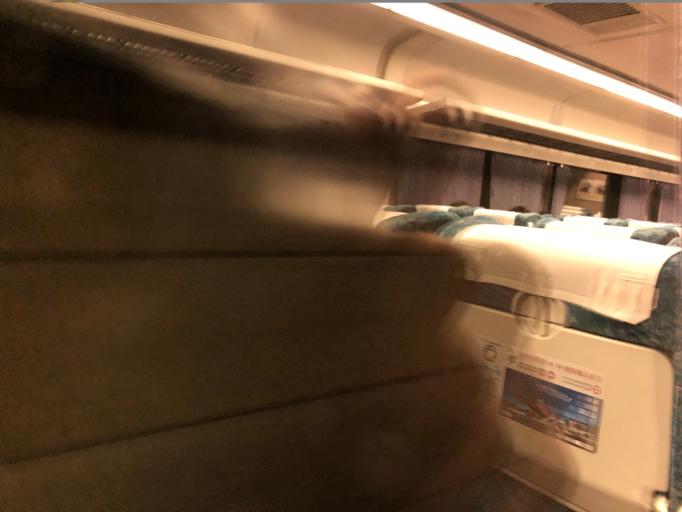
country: JP
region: Kochi
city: Nakamura
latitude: 33.0744
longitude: 133.1043
